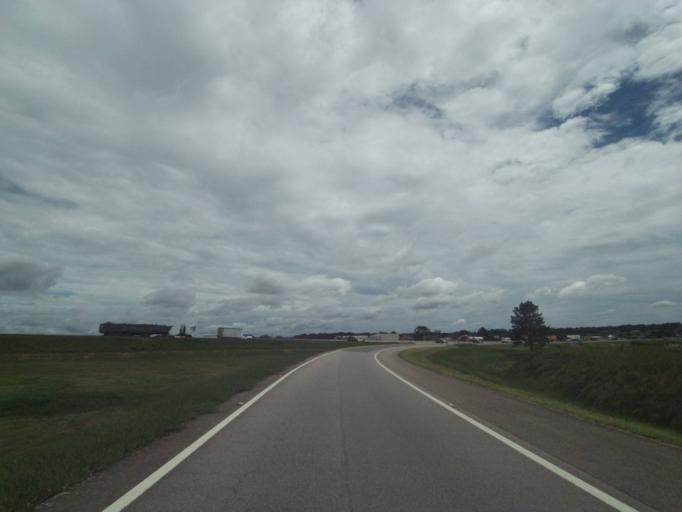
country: BR
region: Parana
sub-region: Sao Jose Dos Pinhais
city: Sao Jose dos Pinhais
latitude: -25.5100
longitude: -49.1258
